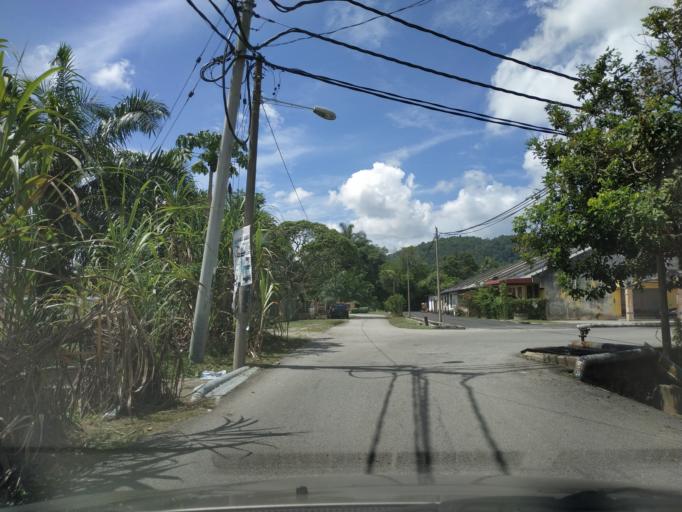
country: MY
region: Perak
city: Parit Buntar
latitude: 5.1380
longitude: 100.5905
